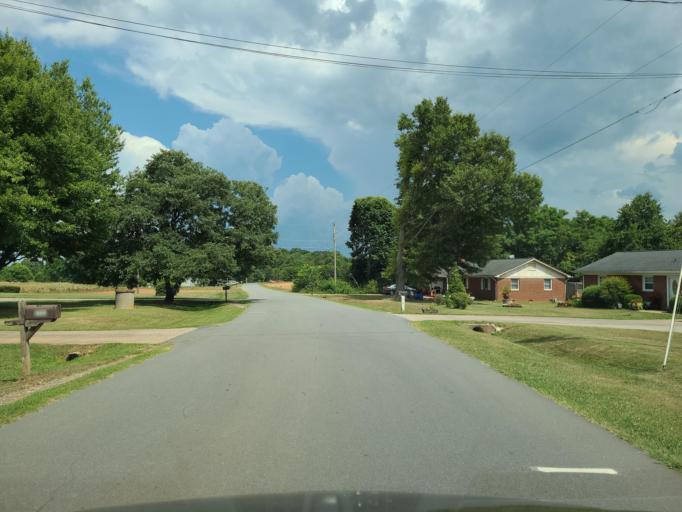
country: US
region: North Carolina
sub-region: Cleveland County
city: Shelby
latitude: 35.2614
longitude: -81.4938
